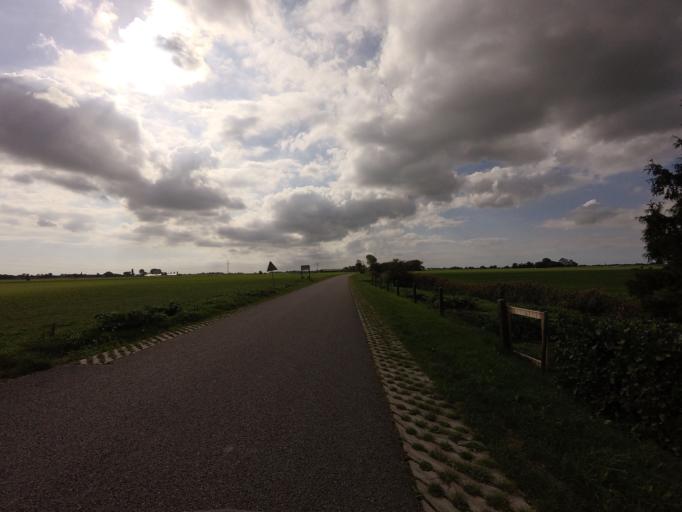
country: NL
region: Friesland
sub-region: Gemeente Littenseradiel
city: Wommels
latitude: 53.0709
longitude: 5.5961
